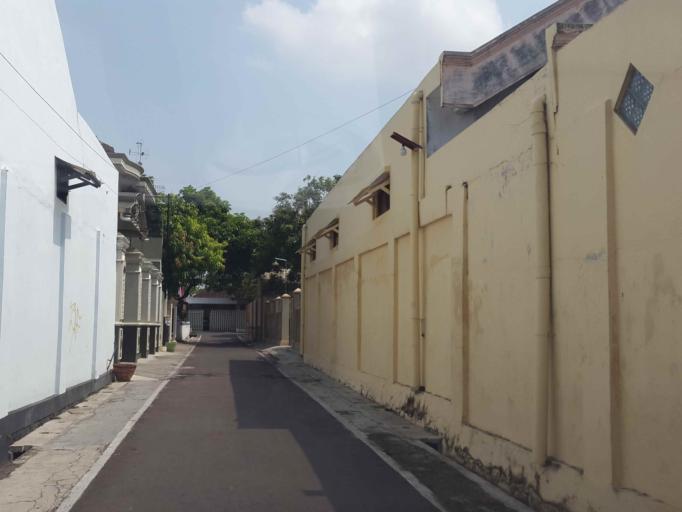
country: ID
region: Central Java
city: Jaten
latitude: -7.5933
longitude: 110.9400
